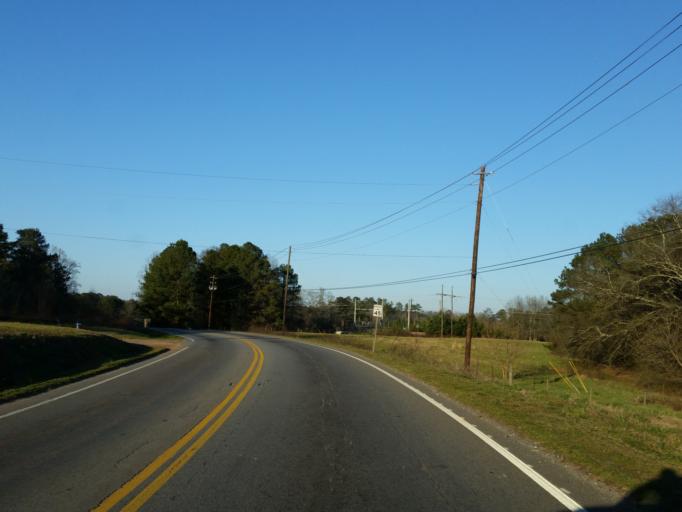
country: US
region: Georgia
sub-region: Cherokee County
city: Woodstock
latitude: 34.1171
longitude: -84.5093
